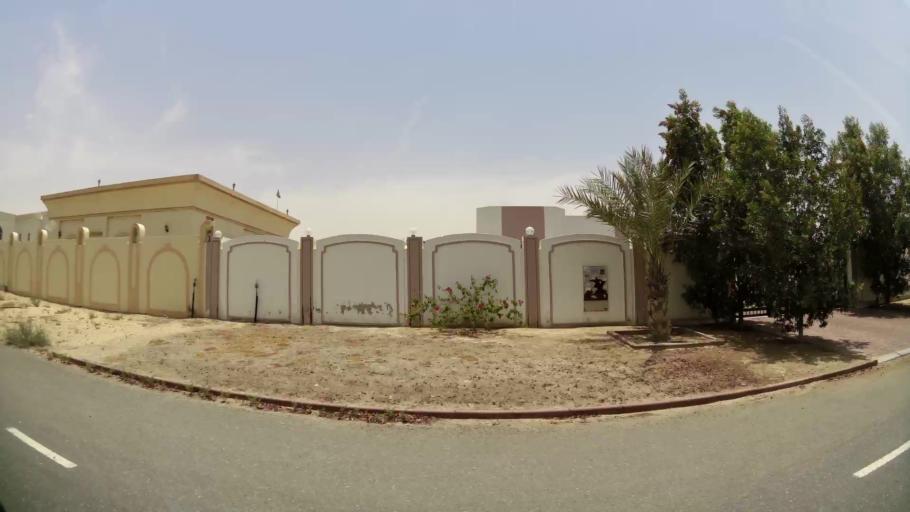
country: AE
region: Ash Shariqah
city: Sharjah
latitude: 25.2071
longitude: 55.3908
